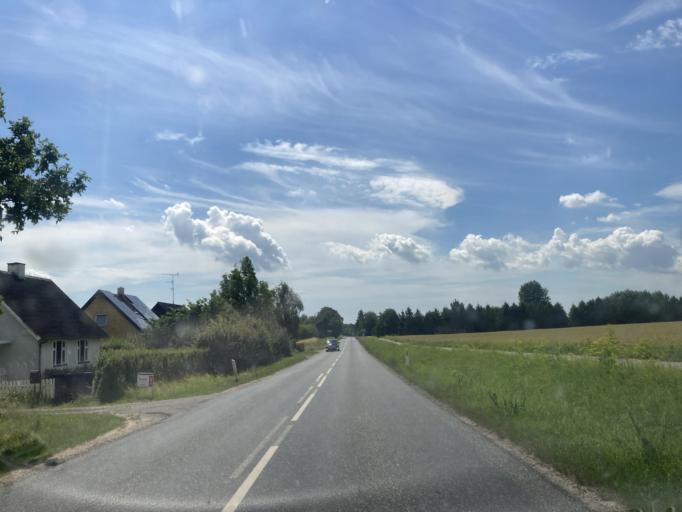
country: DK
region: Zealand
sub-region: Faxe Kommune
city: Haslev
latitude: 55.3728
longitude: 11.9633
